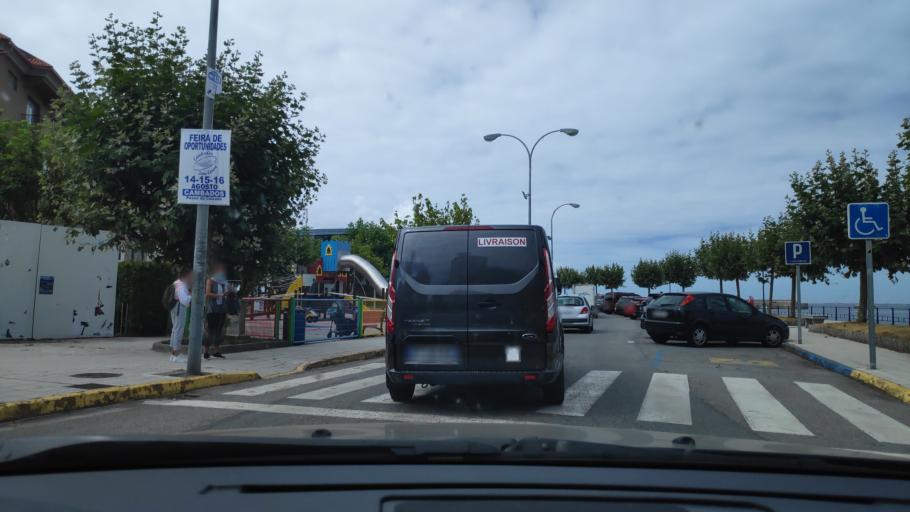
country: ES
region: Galicia
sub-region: Provincia de Pontevedra
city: Cambados
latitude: 42.5155
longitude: -8.8153
